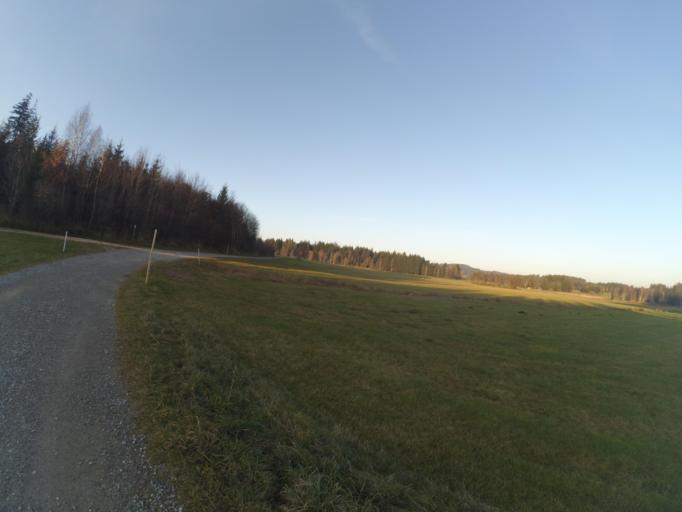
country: DE
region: Bavaria
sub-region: Swabia
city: Aitrang
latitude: 47.8027
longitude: 10.5418
